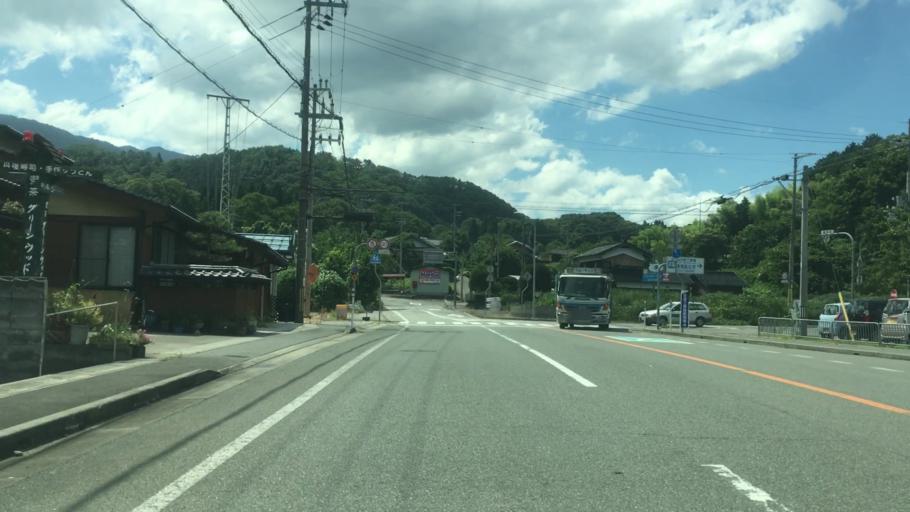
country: JP
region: Hyogo
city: Toyooka
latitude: 35.4872
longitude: 134.6953
